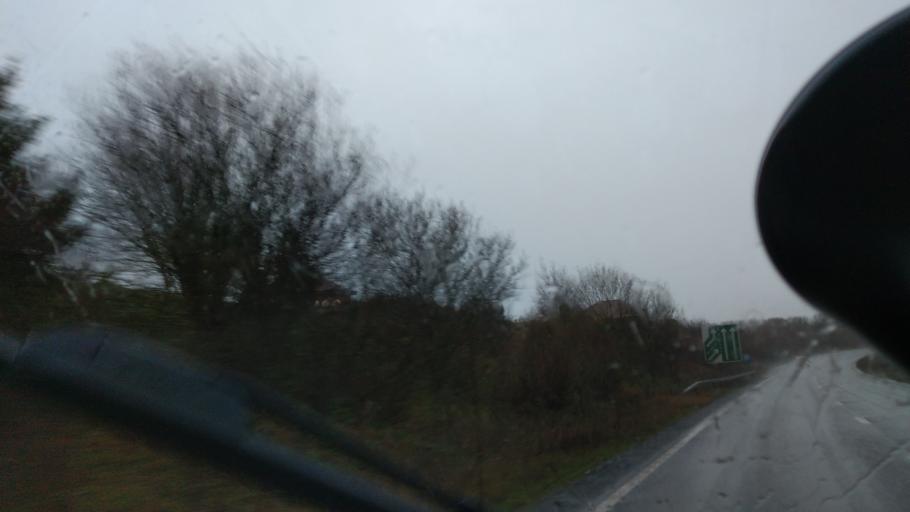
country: GB
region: England
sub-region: West Sussex
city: Shoreham-by-Sea
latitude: 50.8462
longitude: -0.2482
